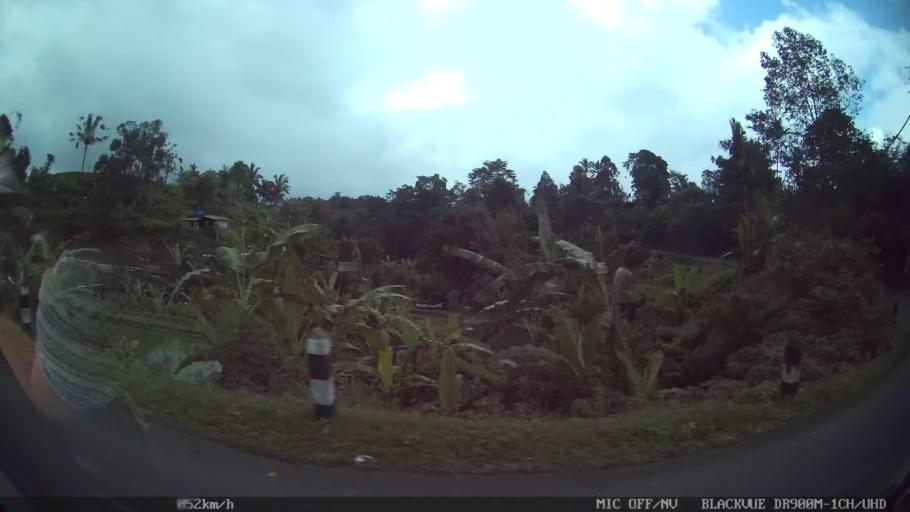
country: ID
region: Bali
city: Empalan
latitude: -8.3795
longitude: 115.1542
